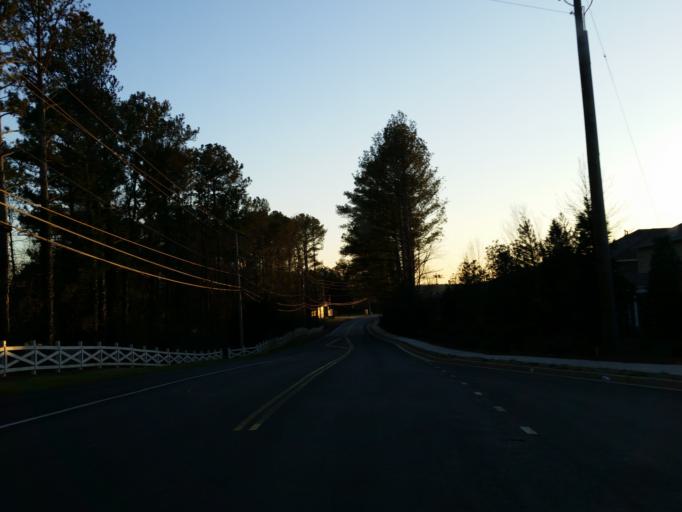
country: US
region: Georgia
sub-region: Cherokee County
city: Woodstock
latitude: 34.1089
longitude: -84.4652
